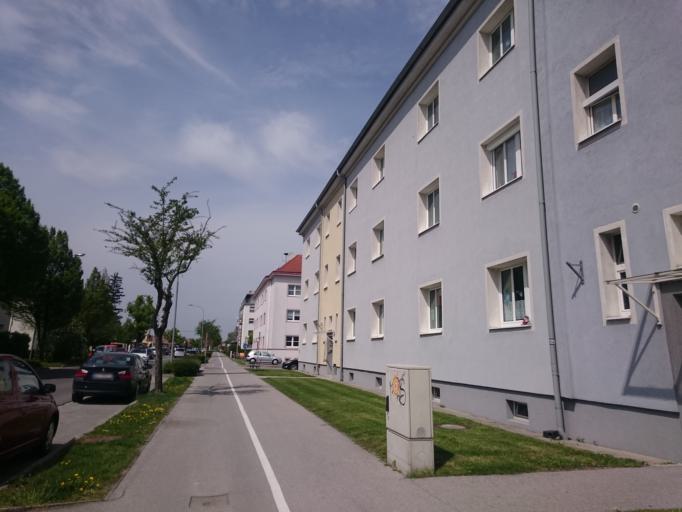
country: AT
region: Lower Austria
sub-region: Politischer Bezirk Korneuburg
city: Korneuburg
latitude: 48.3491
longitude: 16.3270
